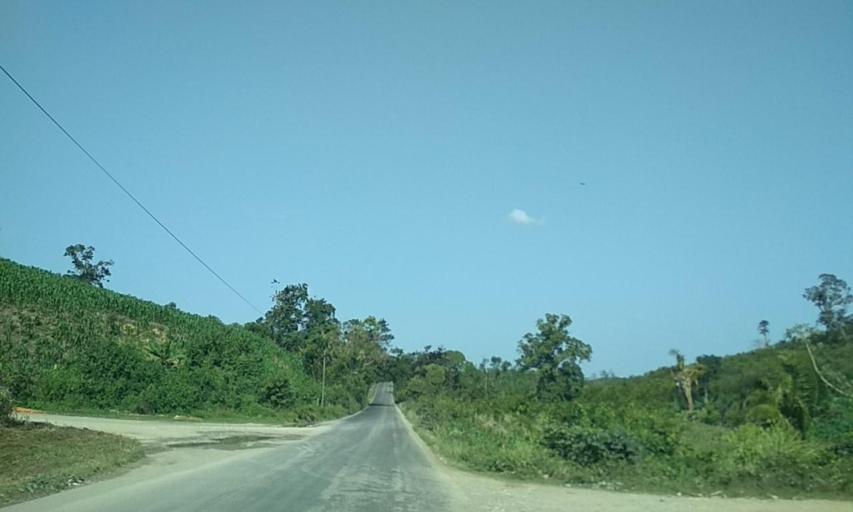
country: MX
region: Veracruz
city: Gutierrez Zamora
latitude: 20.3588
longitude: -97.1593
